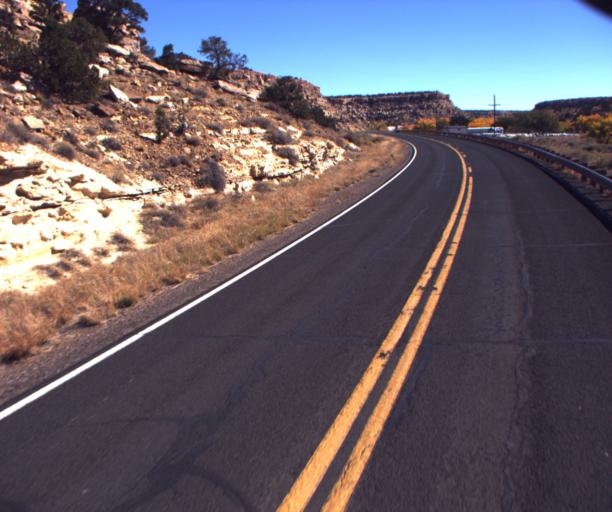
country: US
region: Arizona
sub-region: Navajo County
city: First Mesa
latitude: 35.8170
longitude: -110.2145
